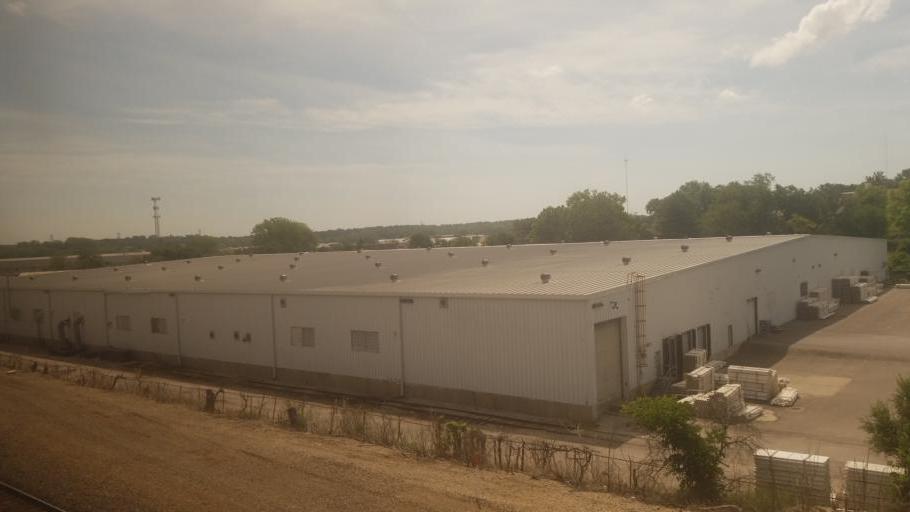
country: US
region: Missouri
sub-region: Clay County
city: North Kansas City
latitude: 39.1076
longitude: -94.5081
